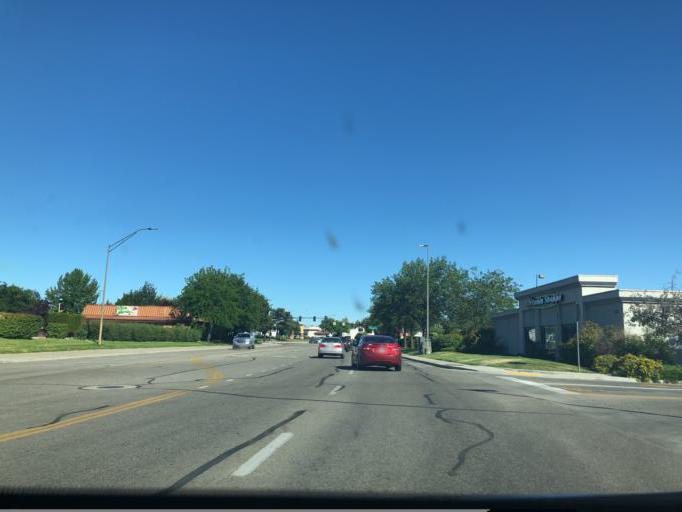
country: US
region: Idaho
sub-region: Ada County
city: Garden City
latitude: 43.6085
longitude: -116.2842
